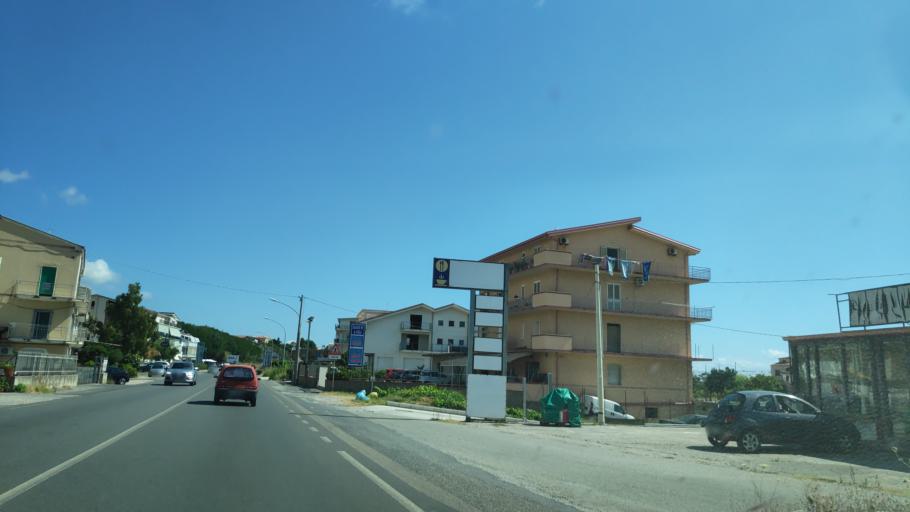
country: IT
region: Calabria
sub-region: Provincia di Cosenza
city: Campora San Giovanni
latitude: 39.0749
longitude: 16.0906
